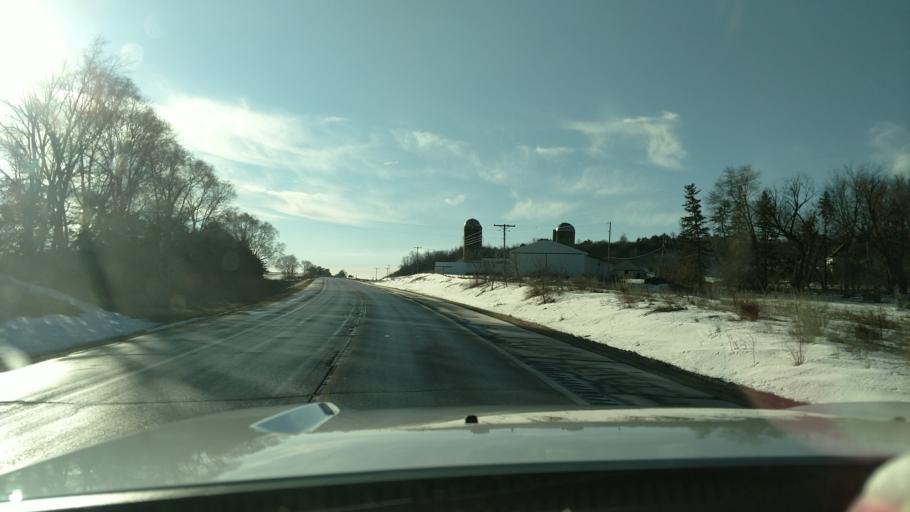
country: US
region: Minnesota
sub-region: Olmsted County
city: Oronoco
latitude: 44.1479
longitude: -92.4186
